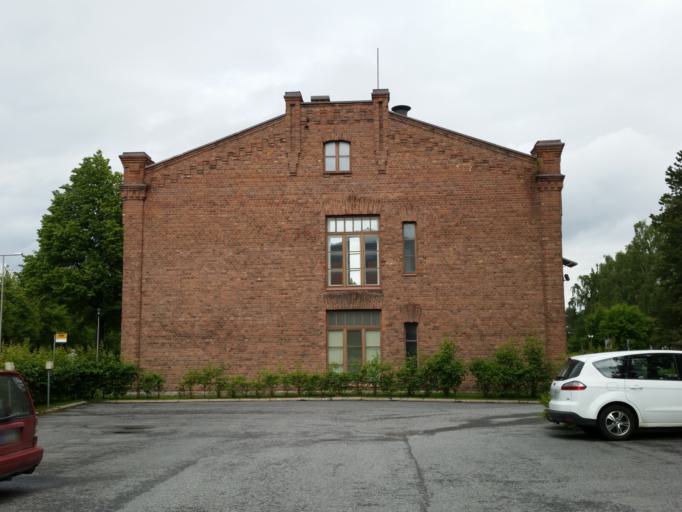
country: FI
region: Northern Savo
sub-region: Kuopio
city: Kuopio
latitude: 62.8947
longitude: 27.6715
